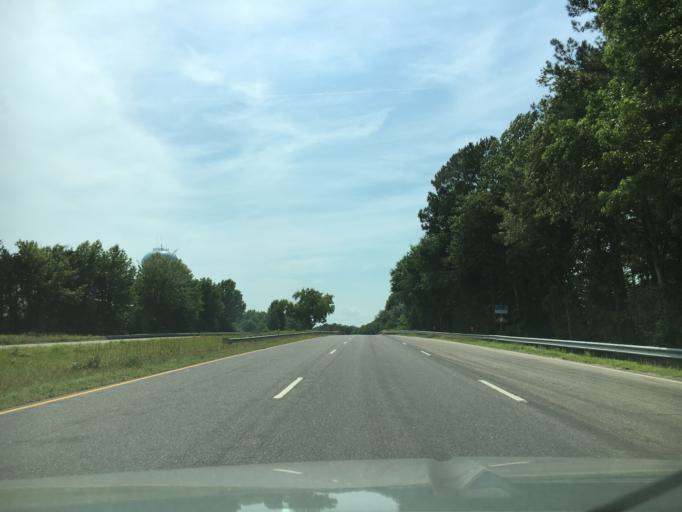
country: US
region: Virginia
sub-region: Amelia County
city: Amelia Court House
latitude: 37.3571
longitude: -77.9660
